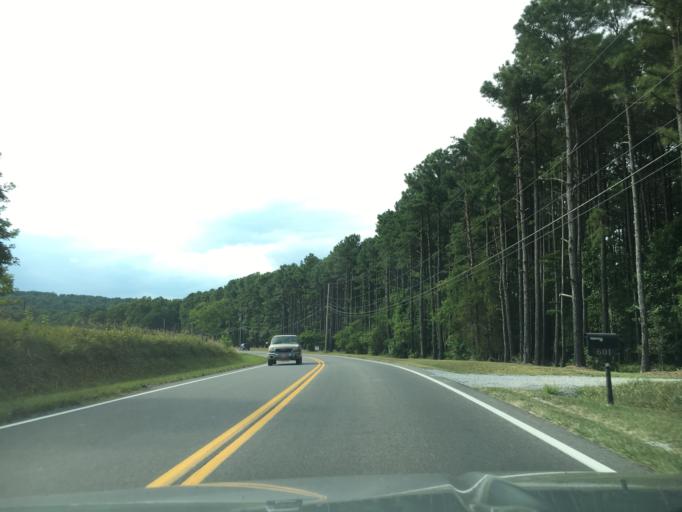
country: US
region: Virginia
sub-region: Campbell County
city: Rustburg
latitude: 37.2695
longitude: -79.1504
